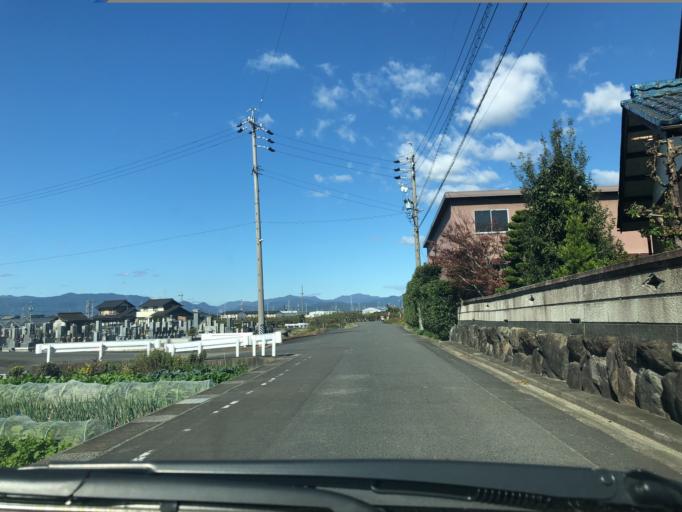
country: JP
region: Gifu
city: Godo
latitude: 35.4087
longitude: 136.6540
